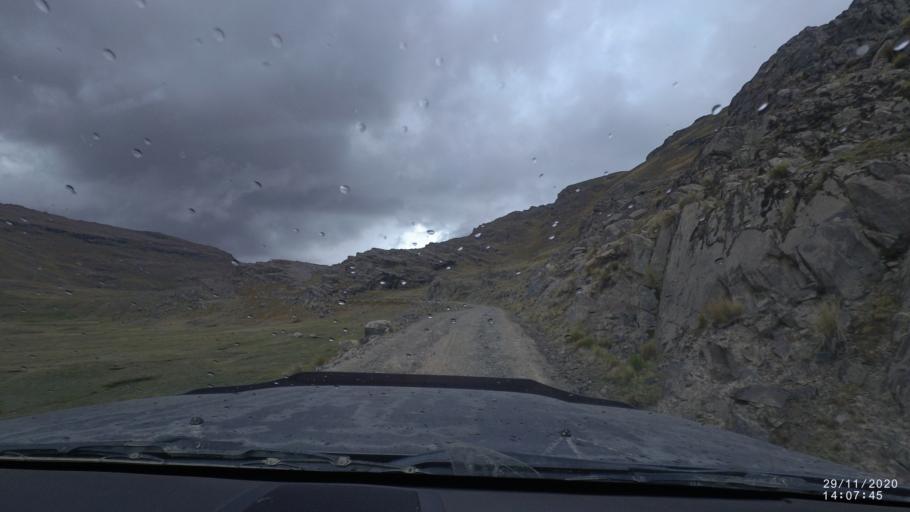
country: BO
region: Cochabamba
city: Sipe Sipe
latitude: -17.2199
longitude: -66.3843
